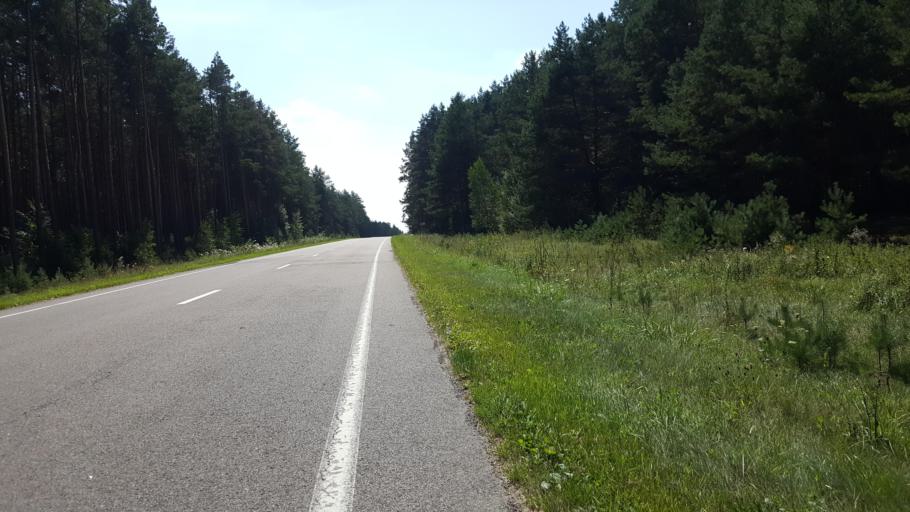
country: PL
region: Podlasie
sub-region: Powiat hajnowski
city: Czeremcha
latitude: 52.5234
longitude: 23.5352
